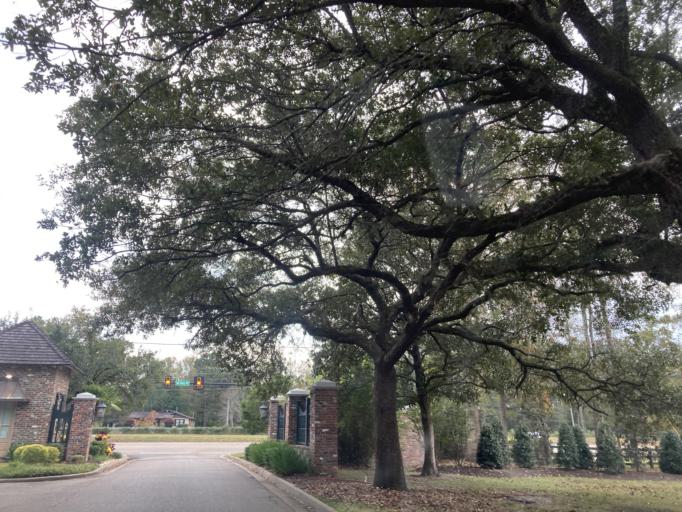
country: US
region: Mississippi
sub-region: Lamar County
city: West Hattiesburg
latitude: 31.3149
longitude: -89.4568
